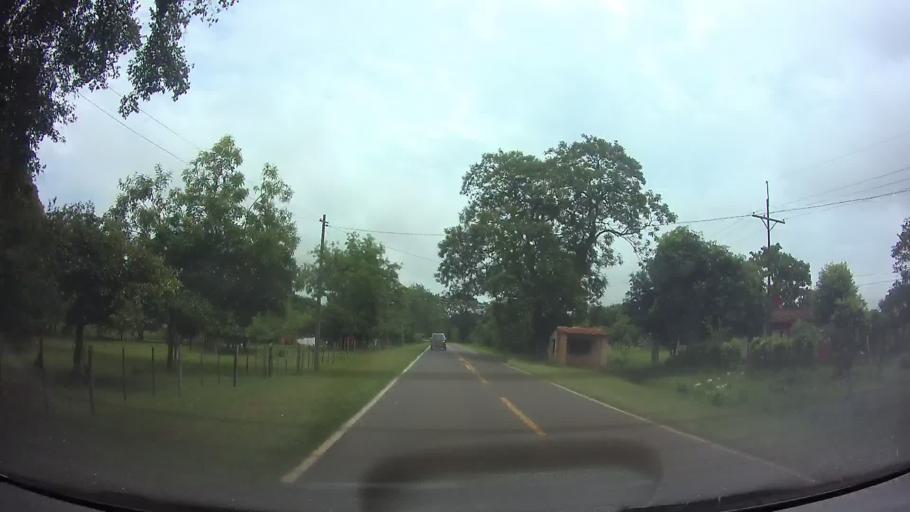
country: PY
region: Paraguari
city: Ybycui
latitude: -25.9676
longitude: -57.0814
